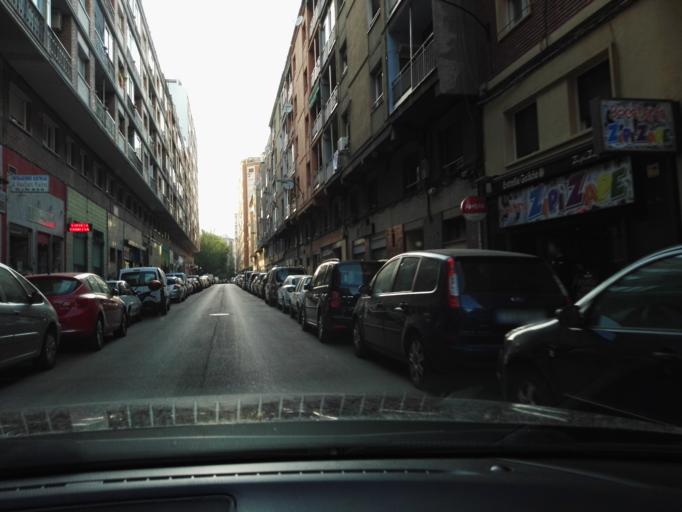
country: ES
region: Aragon
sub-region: Provincia de Zaragoza
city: Zaragoza
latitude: 41.6384
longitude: -0.8797
